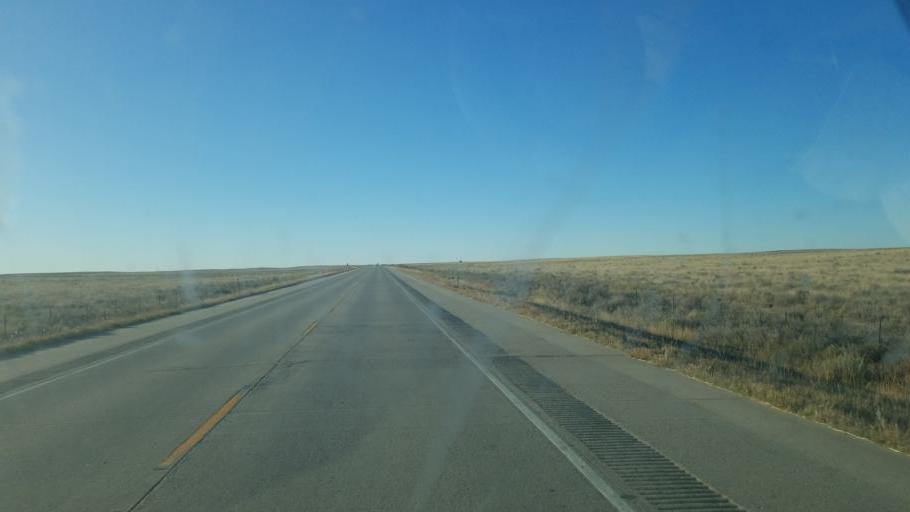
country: US
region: Colorado
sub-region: Kiowa County
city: Eads
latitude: 38.5624
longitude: -102.7861
